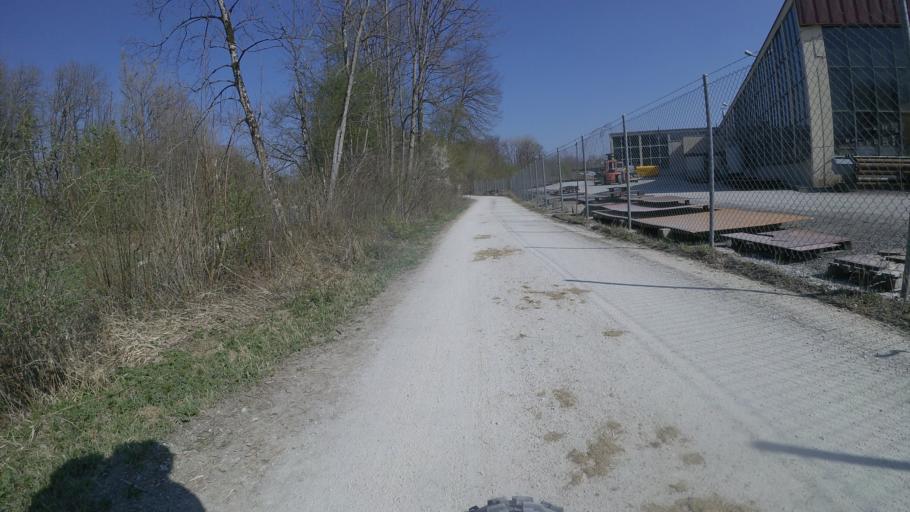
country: DE
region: Bavaria
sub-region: Upper Bavaria
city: Traunreut
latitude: 47.9449
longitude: 12.5887
